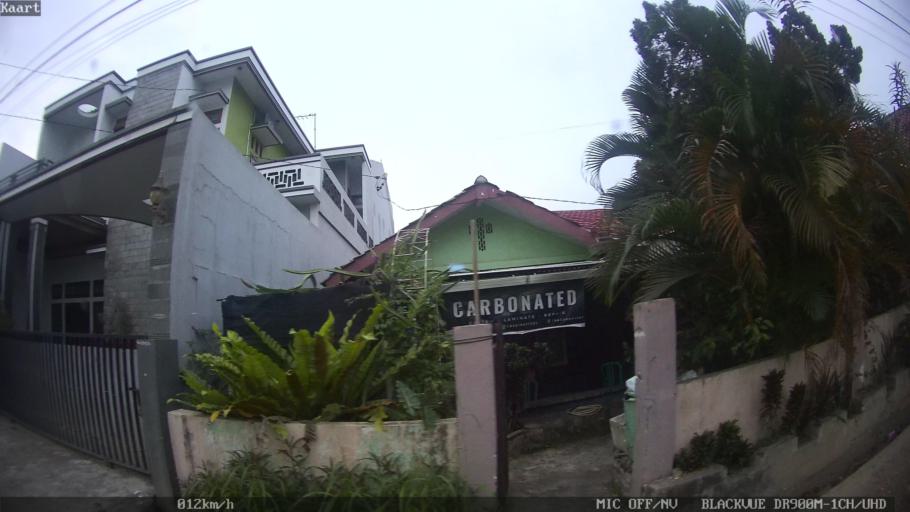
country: ID
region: Lampung
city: Kedaton
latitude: -5.4041
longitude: 105.2644
